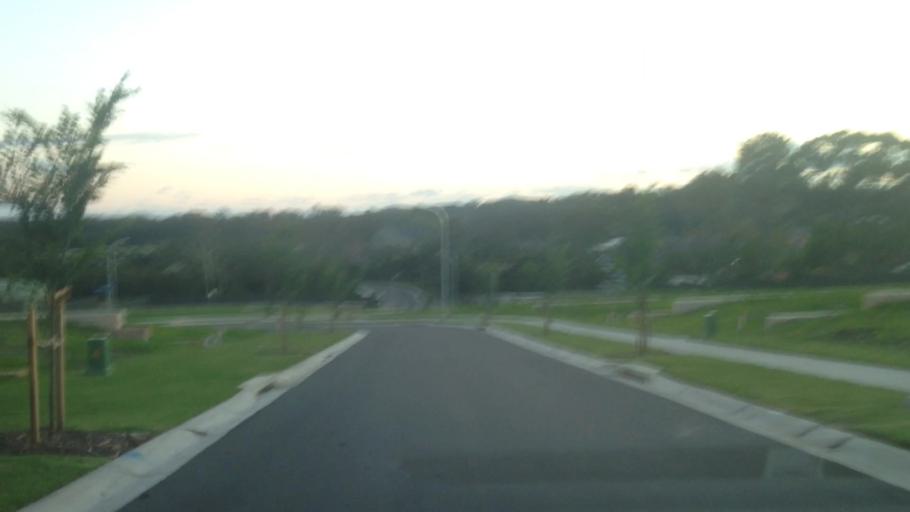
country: AU
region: New South Wales
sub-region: Lake Macquarie Shire
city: Cooranbong
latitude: -33.0703
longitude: 151.4567
